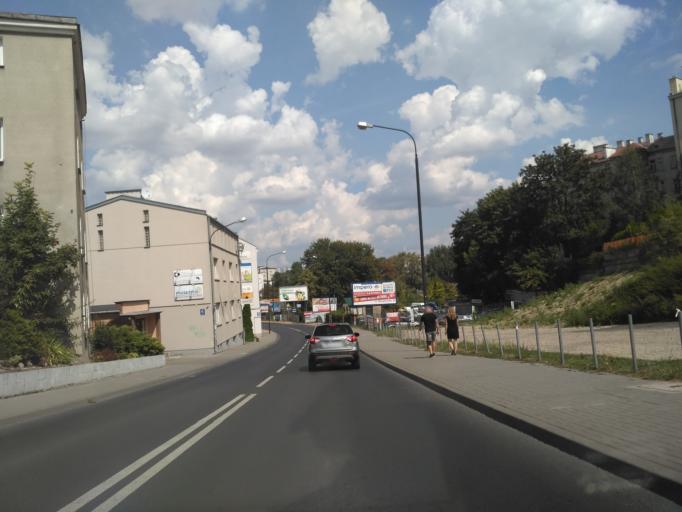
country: PL
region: Lublin Voivodeship
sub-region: Powiat lubelski
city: Lublin
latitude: 51.2516
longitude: 22.5594
